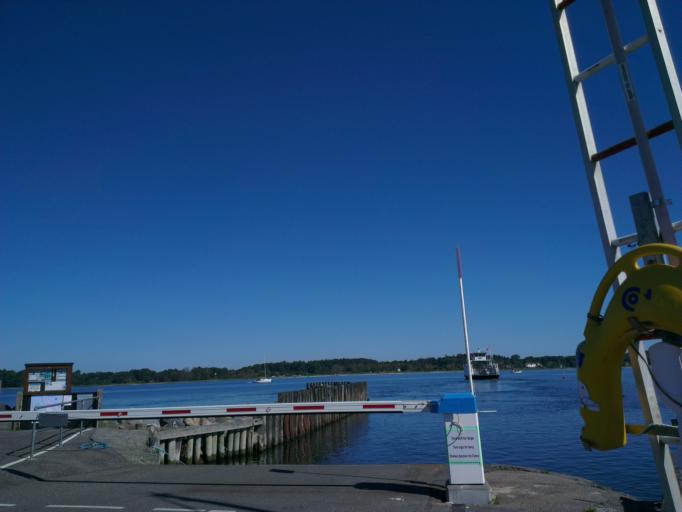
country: DK
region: Capital Region
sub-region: Halsnaes Kommune
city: Hundested
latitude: 55.9372
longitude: 11.9054
